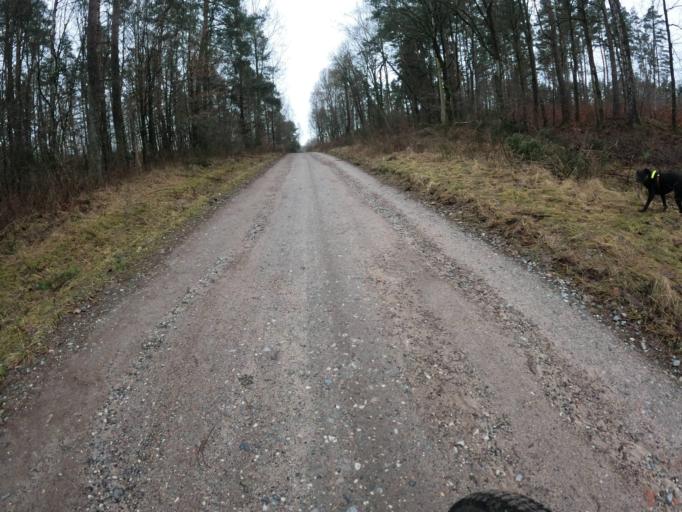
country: PL
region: West Pomeranian Voivodeship
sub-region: Powiat slawienski
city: Slawno
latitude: 54.2421
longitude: 16.6450
